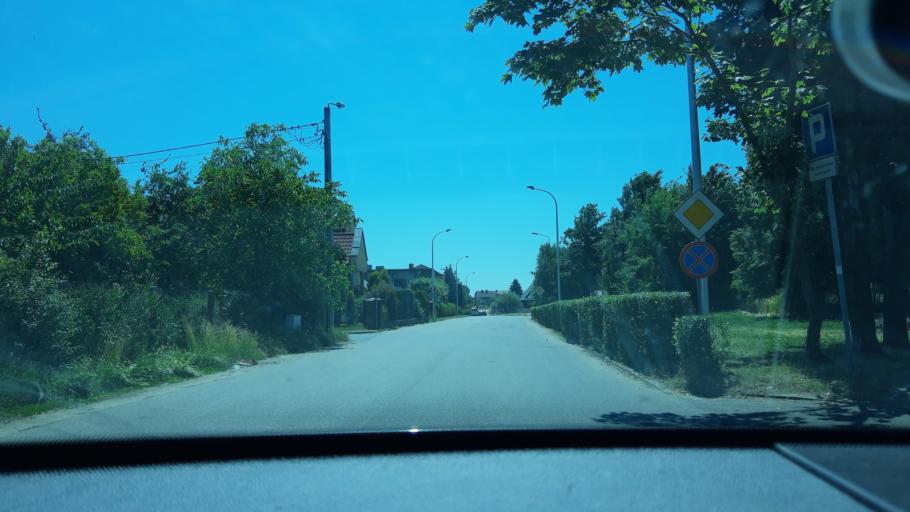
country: PL
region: Lodz Voivodeship
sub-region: Powiat sieradzki
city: Sieradz
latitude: 51.5874
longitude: 18.7322
